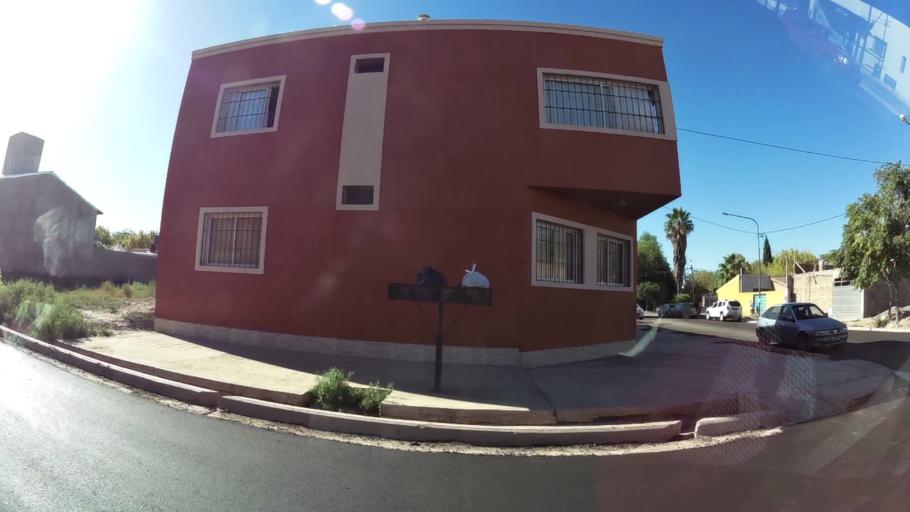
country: AR
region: Mendoza
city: Las Heras
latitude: -32.8487
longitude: -68.8290
